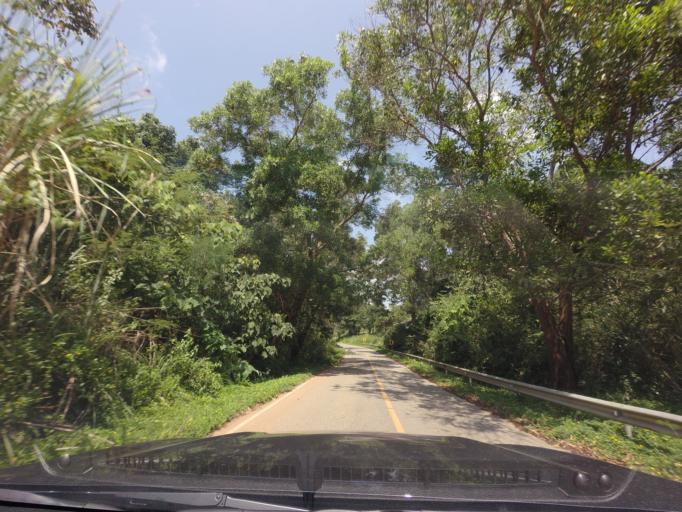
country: TH
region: Loei
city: Na Haeo
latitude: 17.6036
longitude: 100.8944
